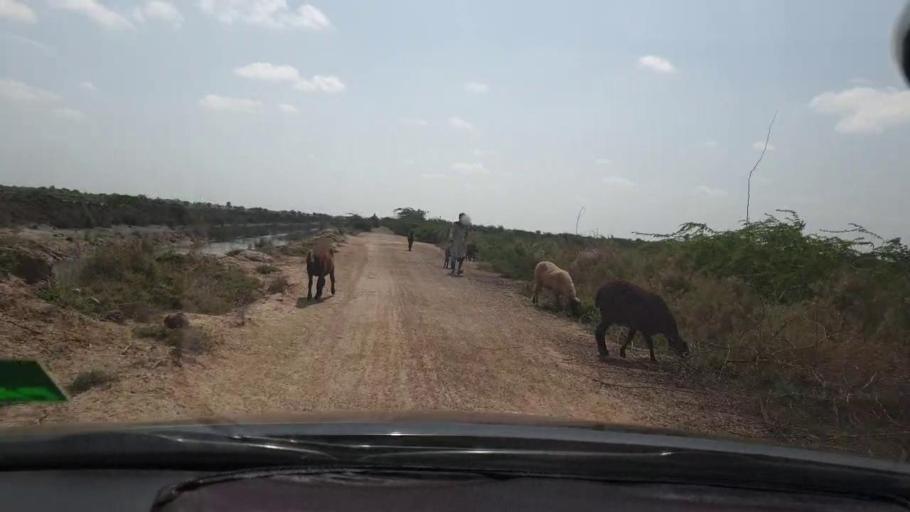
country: PK
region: Sindh
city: Tando Bago
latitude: 24.8302
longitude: 69.0593
